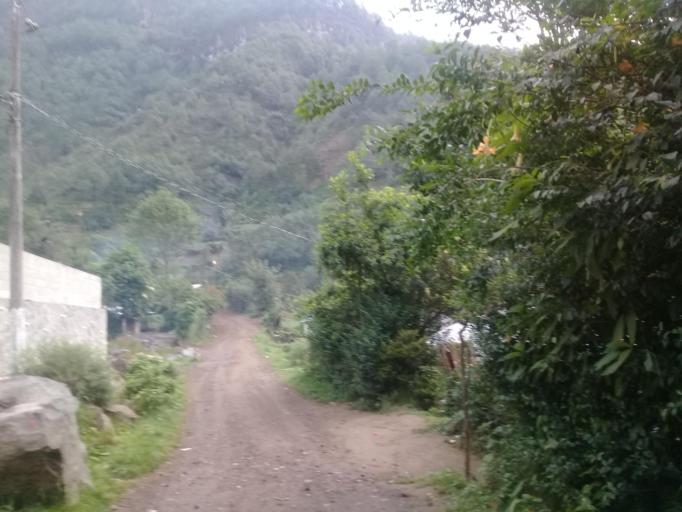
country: MX
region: Veracruz
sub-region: Mariano Escobedo
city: San Isidro el Berro
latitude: 18.9574
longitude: -97.1968
